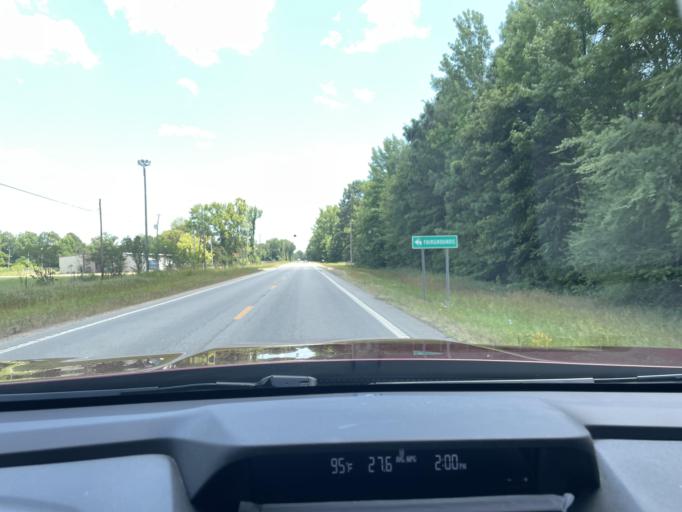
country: US
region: Arkansas
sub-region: Drew County
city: Monticello
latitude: 33.6122
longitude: -91.7410
